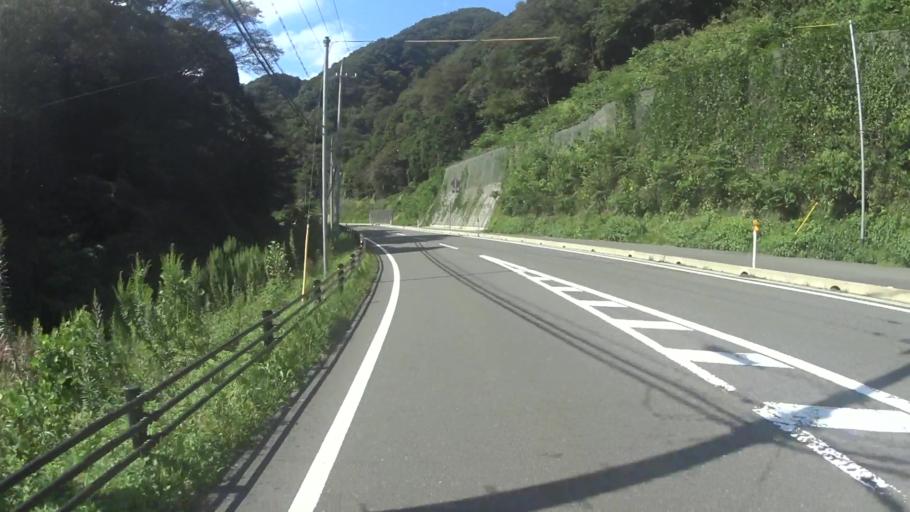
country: JP
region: Kyoto
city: Miyazu
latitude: 35.6863
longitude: 135.2896
